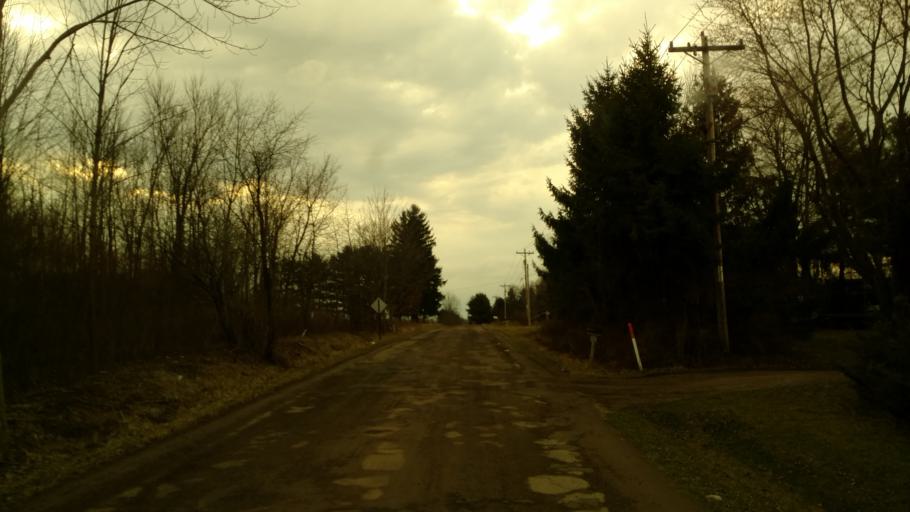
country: US
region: Ohio
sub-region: Richland County
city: Lexington
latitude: 40.6520
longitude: -82.6658
